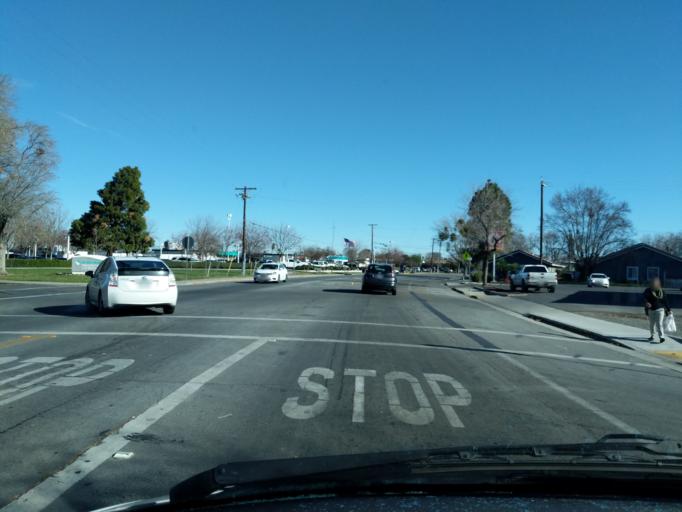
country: US
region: California
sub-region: Merced County
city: Los Banos
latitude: 37.0631
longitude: -120.8609
